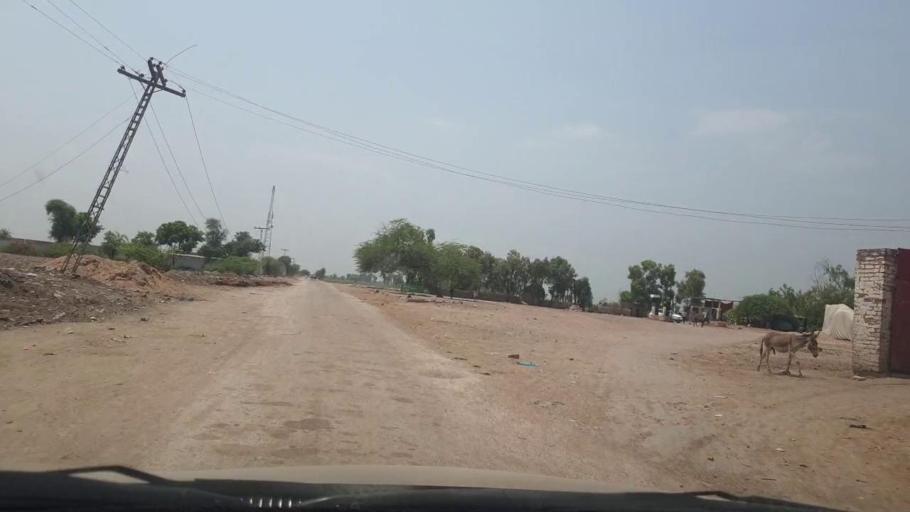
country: PK
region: Sindh
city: Ratodero
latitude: 27.7226
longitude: 68.2804
